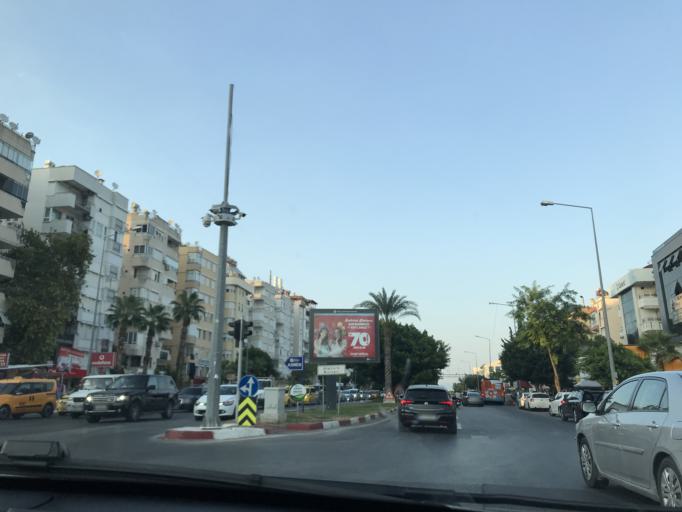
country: TR
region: Antalya
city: Antalya
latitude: 36.8651
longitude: 30.6338
